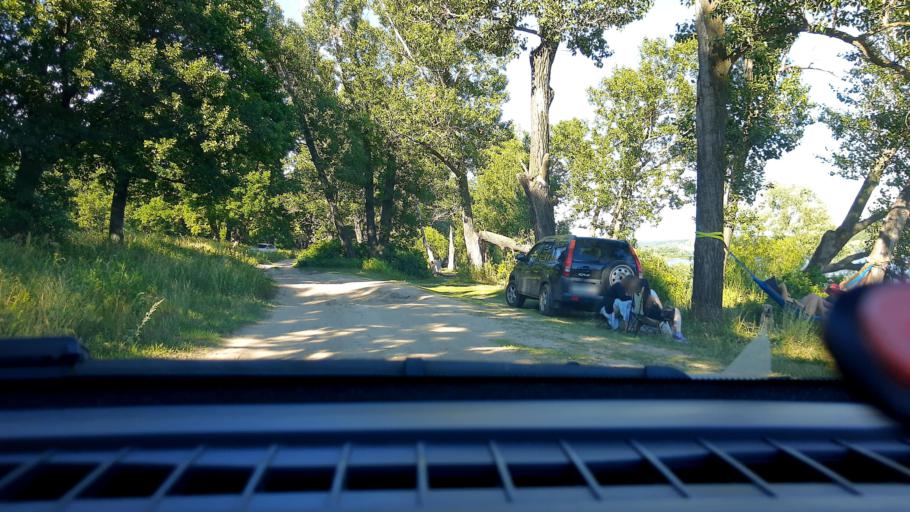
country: RU
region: Nizjnij Novgorod
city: Burevestnik
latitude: 56.2024
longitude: 43.8306
